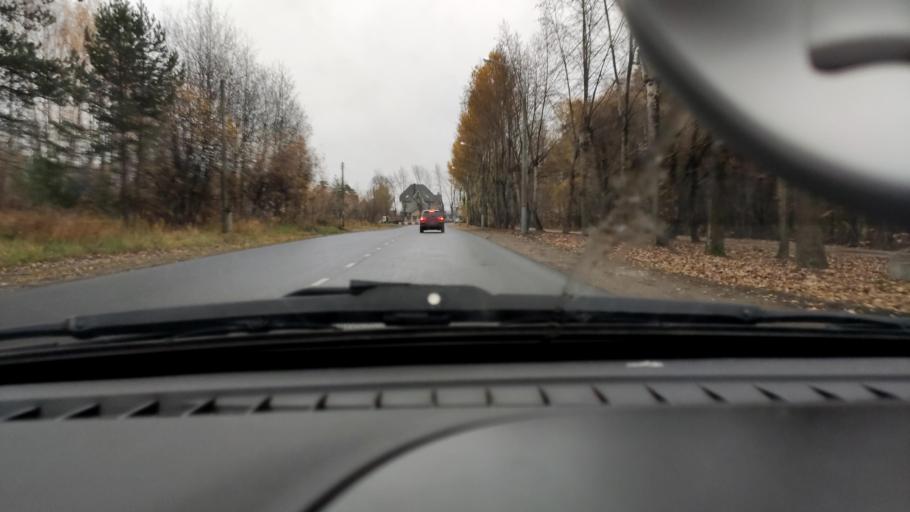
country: RU
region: Perm
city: Kultayevo
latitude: 58.0144
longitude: 55.9829
